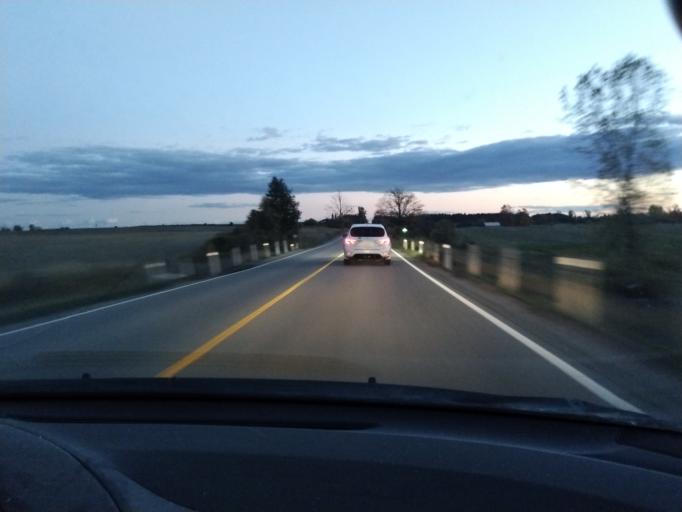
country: CA
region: Ontario
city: Bradford West Gwillimbury
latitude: 44.1383
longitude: -79.6489
